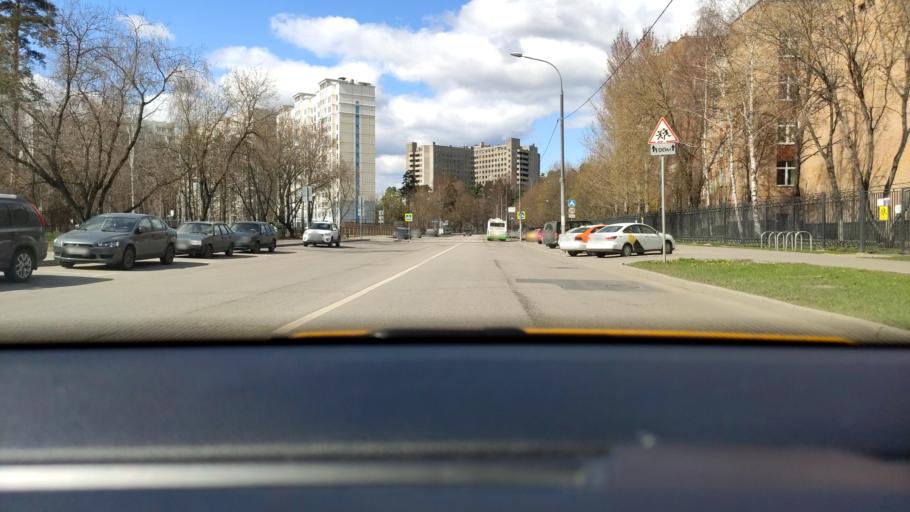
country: RU
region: Moscow
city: Yaroslavskiy
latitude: 55.8854
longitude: 37.7093
